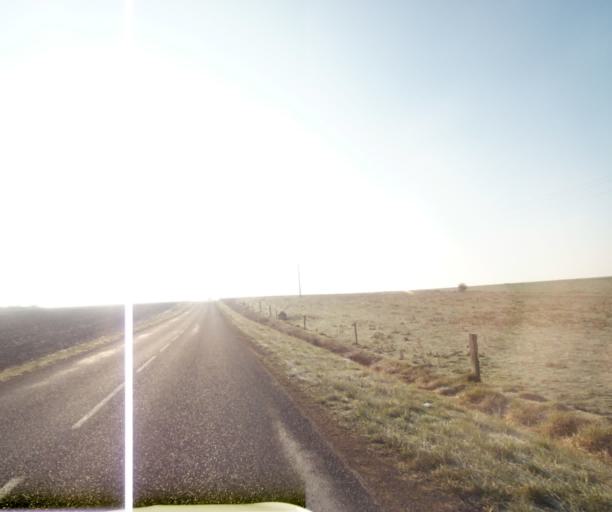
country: FR
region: Champagne-Ardenne
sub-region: Departement de la Haute-Marne
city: Montier-en-Der
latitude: 48.5028
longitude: 4.7499
